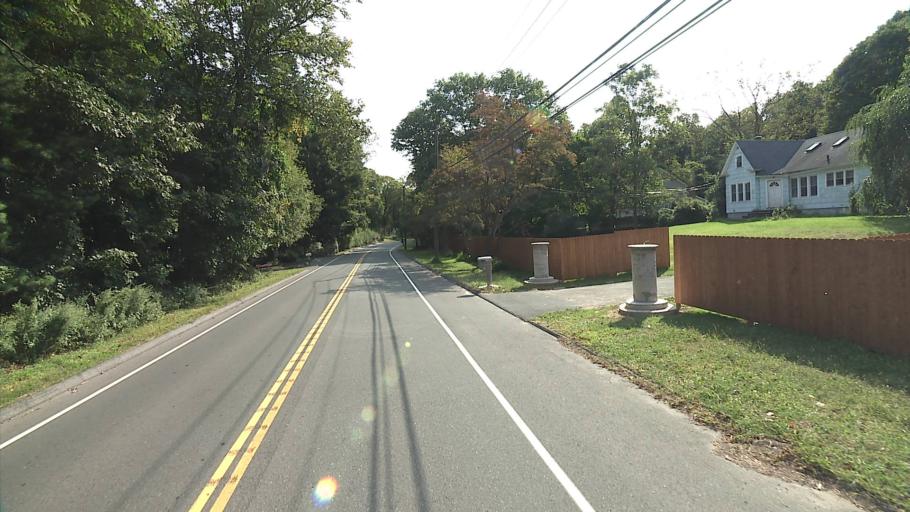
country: US
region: Connecticut
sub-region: Fairfield County
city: Fairfield
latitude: 41.2042
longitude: -73.2761
